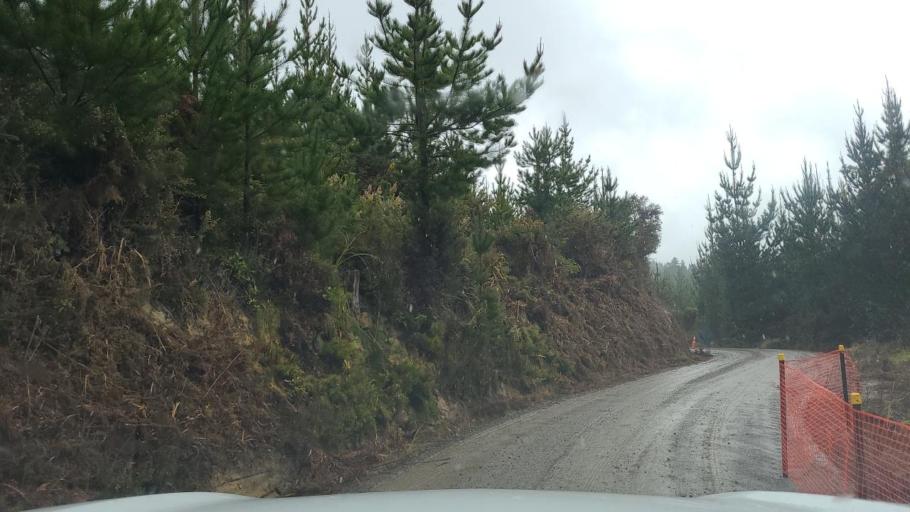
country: NZ
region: Wellington
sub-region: Masterton District
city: Masterton
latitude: -41.1765
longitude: 175.8681
